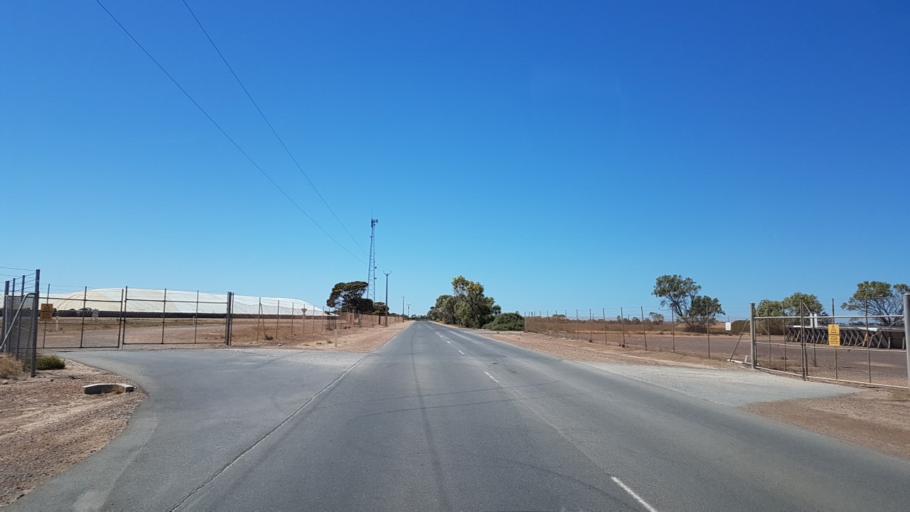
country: AU
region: South Australia
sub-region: Copper Coast
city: Wallaroo
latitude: -33.9400
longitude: 137.6128
